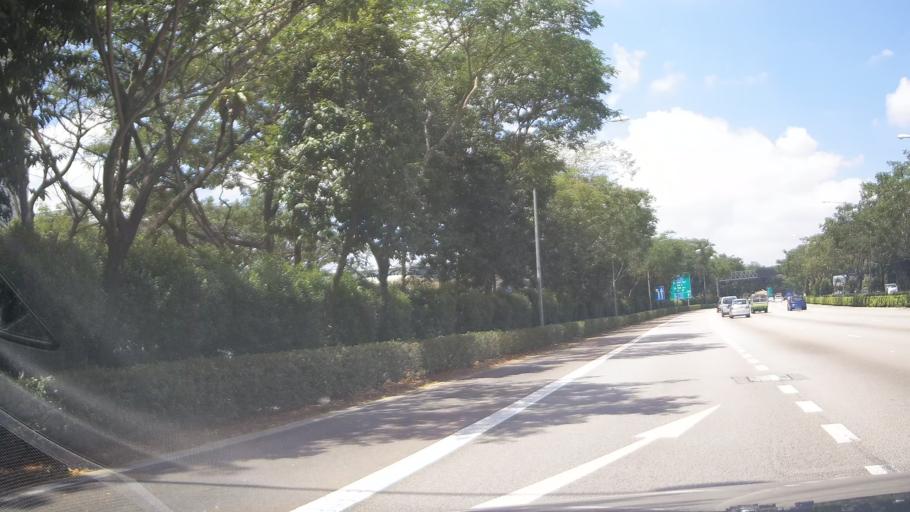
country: SG
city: Singapore
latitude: 1.3347
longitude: 103.7742
